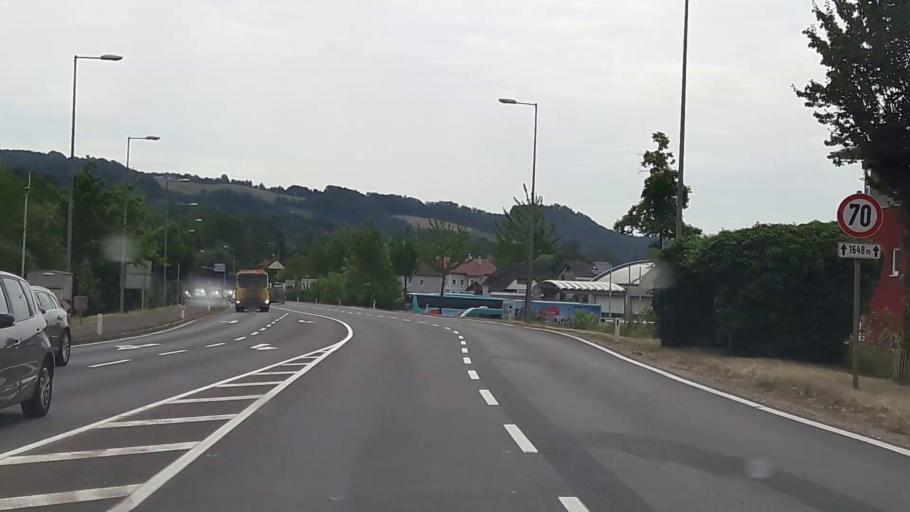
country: AT
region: Upper Austria
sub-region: Politischer Bezirk Urfahr-Umgebung
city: Ottensheim
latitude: 48.3372
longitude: 14.1767
